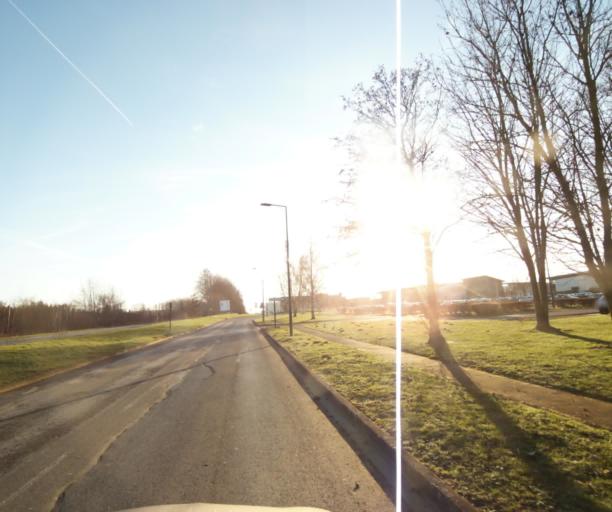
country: FR
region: Nord-Pas-de-Calais
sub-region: Departement du Nord
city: Famars
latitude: 50.3235
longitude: 3.5162
